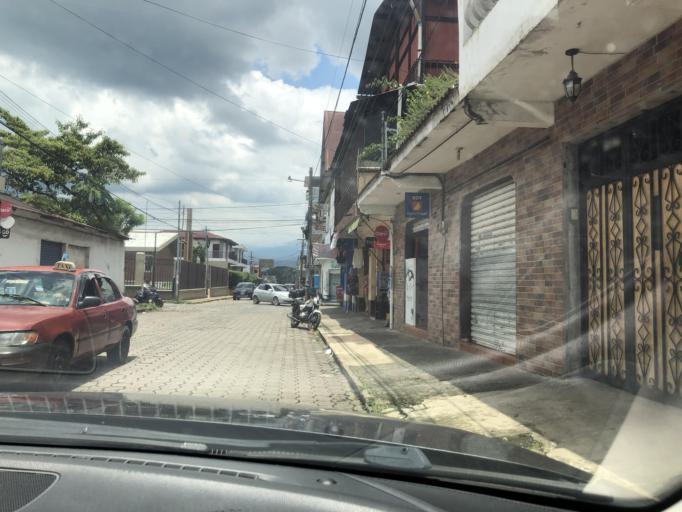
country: GT
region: Quetzaltenango
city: Coatepeque
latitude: 14.7072
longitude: -91.8650
